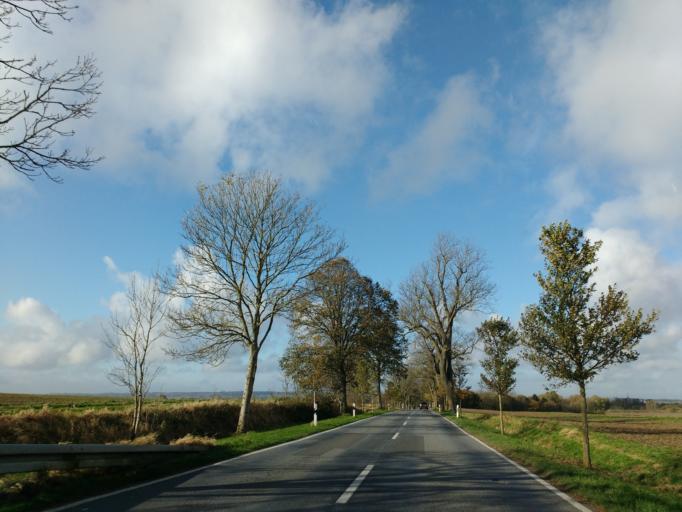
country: DE
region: Mecklenburg-Vorpommern
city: Klutz
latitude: 53.9618
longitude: 11.1840
